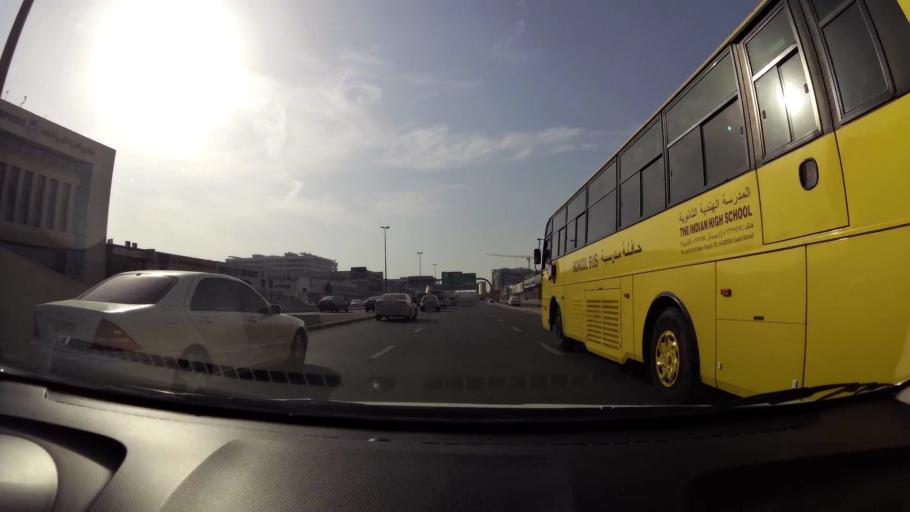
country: AE
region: Ash Shariqah
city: Sharjah
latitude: 25.2548
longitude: 55.3391
